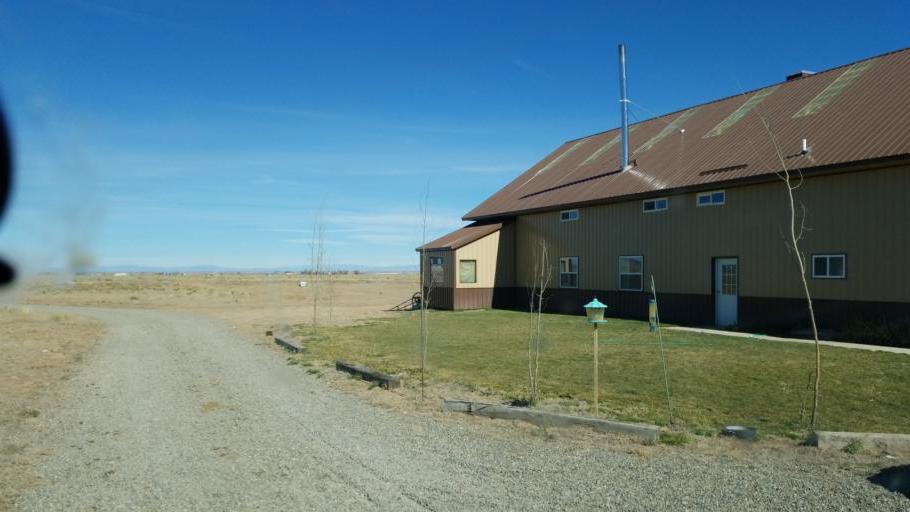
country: US
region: Colorado
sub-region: Rio Grande County
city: Monte Vista
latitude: 37.3994
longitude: -106.1190
